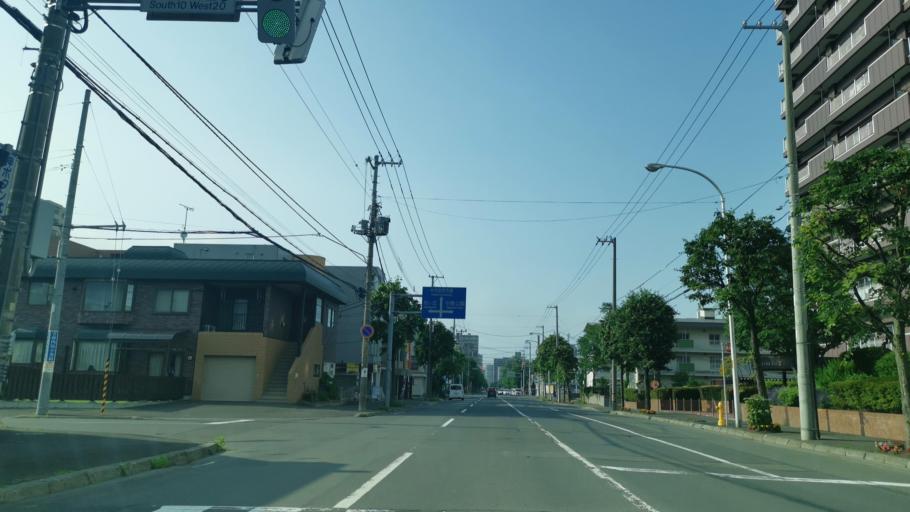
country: JP
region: Hokkaido
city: Sapporo
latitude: 43.0462
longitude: 141.3289
